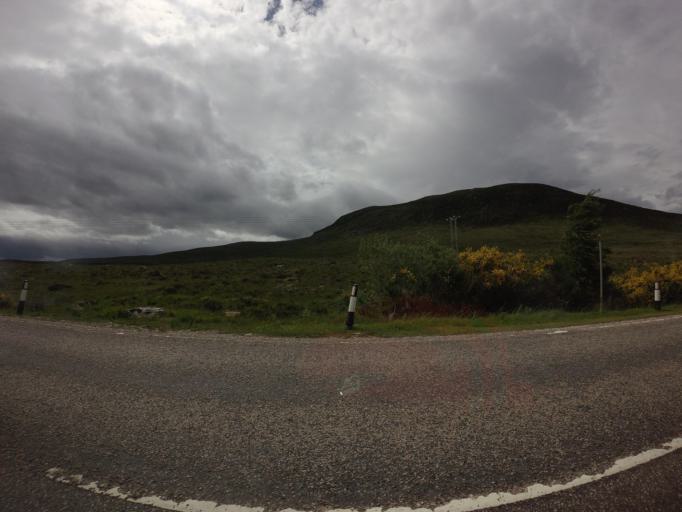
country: GB
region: Scotland
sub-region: Highland
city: Ullapool
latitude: 57.7162
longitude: -4.8650
